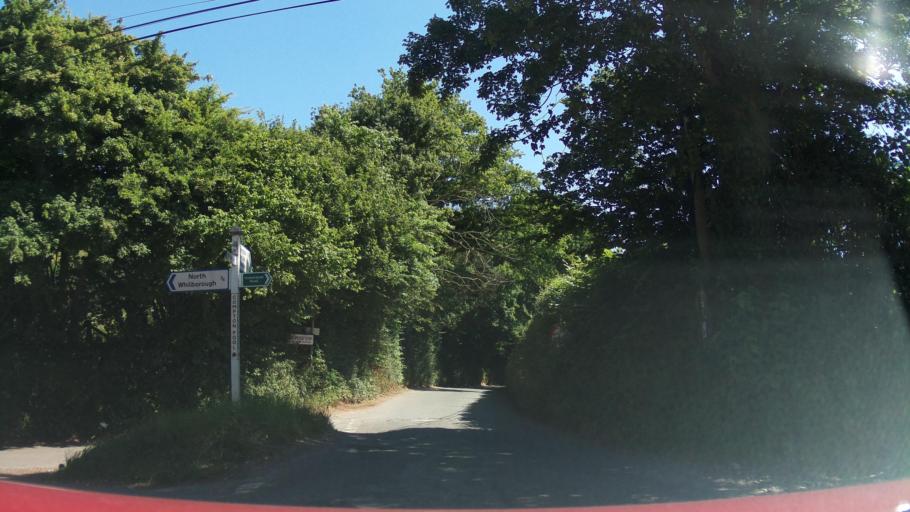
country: GB
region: England
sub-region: Devon
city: Marldon
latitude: 50.4794
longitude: -3.6036
